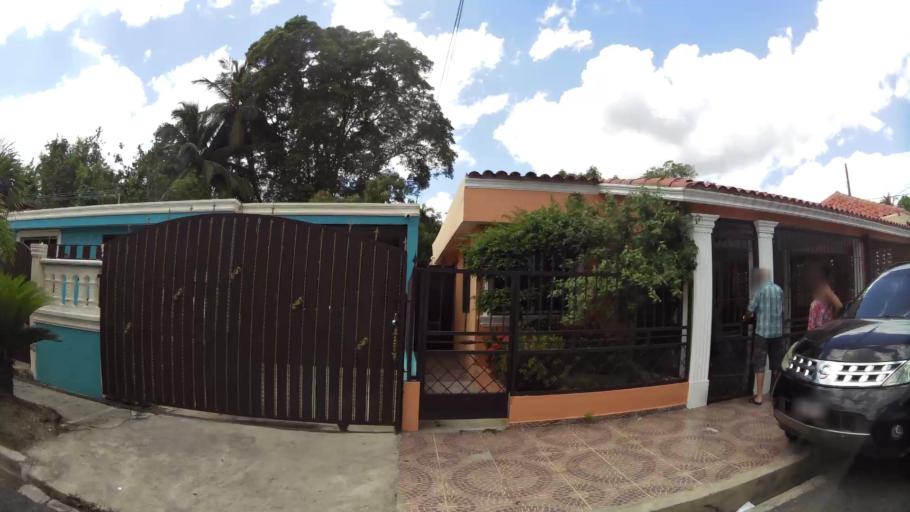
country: DO
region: Nacional
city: Ensanche Luperon
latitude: 18.5181
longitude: -69.9108
